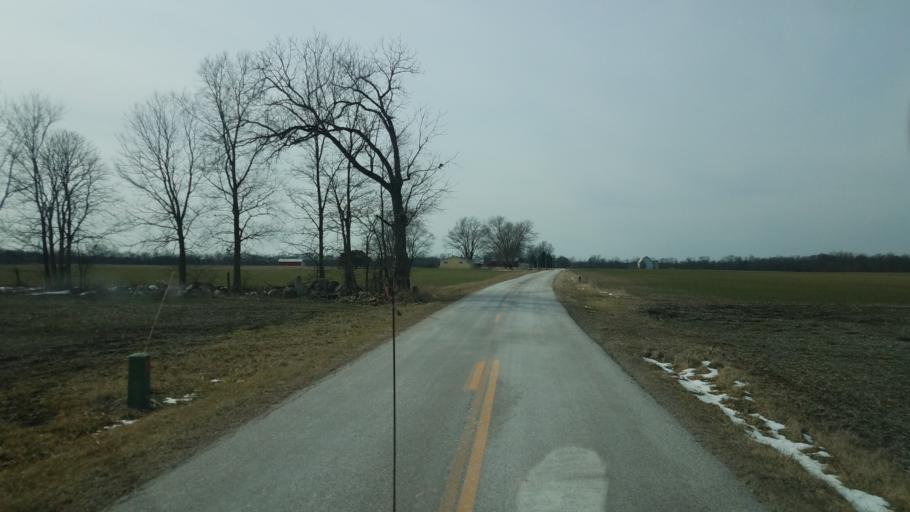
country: US
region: Ohio
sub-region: Marion County
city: Prospect
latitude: 40.3654
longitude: -83.1725
